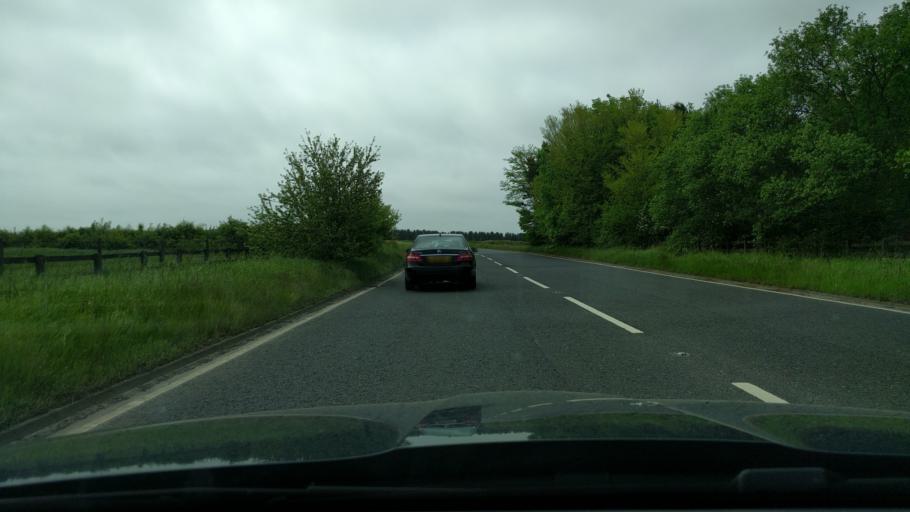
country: GB
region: England
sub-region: Northumberland
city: East Chevington
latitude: 55.2647
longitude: -1.6059
